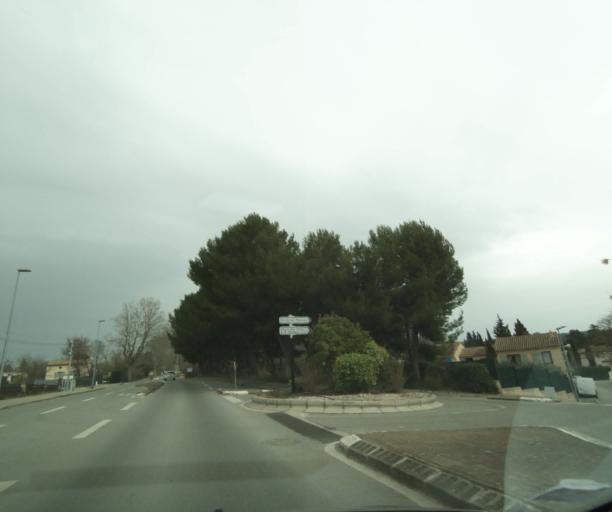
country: FR
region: Provence-Alpes-Cote d'Azur
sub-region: Departement des Bouches-du-Rhone
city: Aix-en-Provence
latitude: 43.5573
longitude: 5.4604
